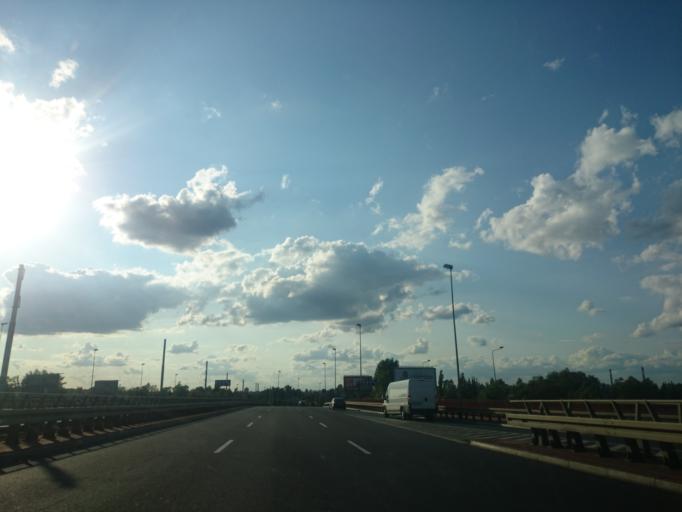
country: PL
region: West Pomeranian Voivodeship
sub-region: Szczecin
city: Szczecin
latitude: 53.3963
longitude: 14.6052
